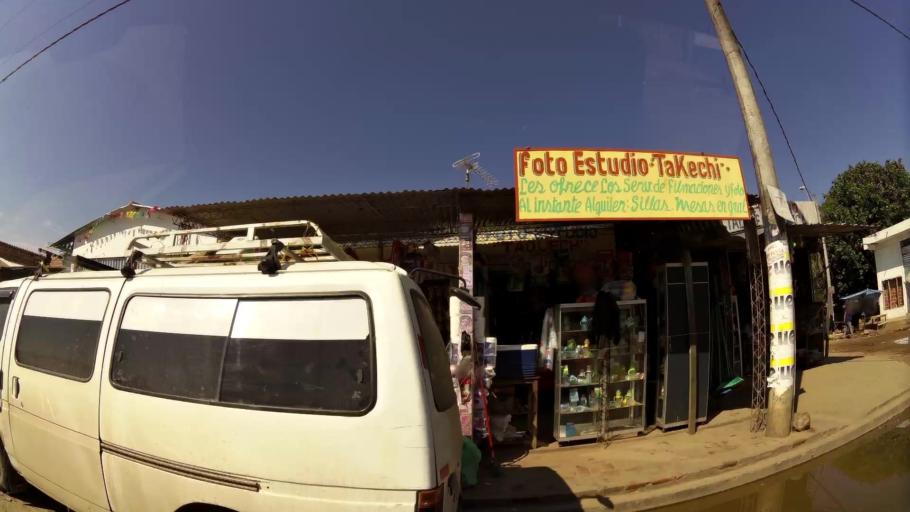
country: BO
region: Santa Cruz
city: Cotoca
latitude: -17.7402
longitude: -63.0741
